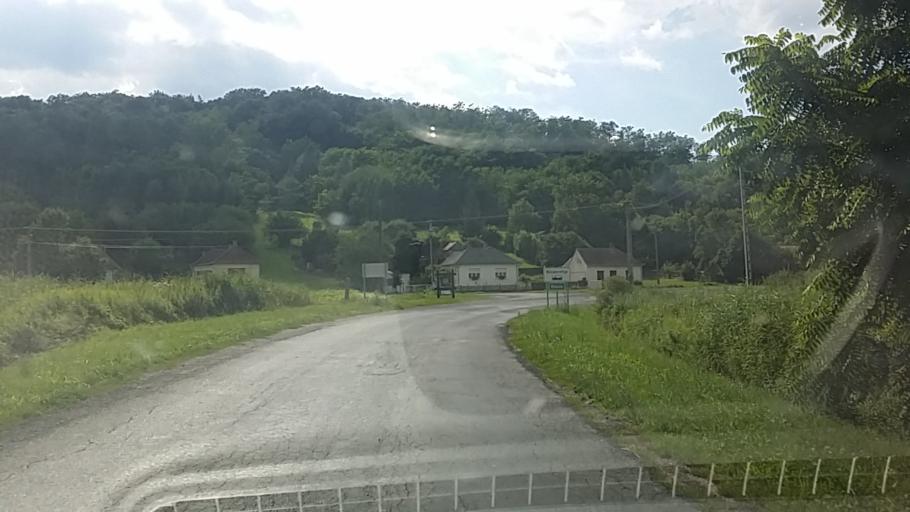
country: HU
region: Zala
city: Becsehely
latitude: 46.5253
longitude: 16.7563
